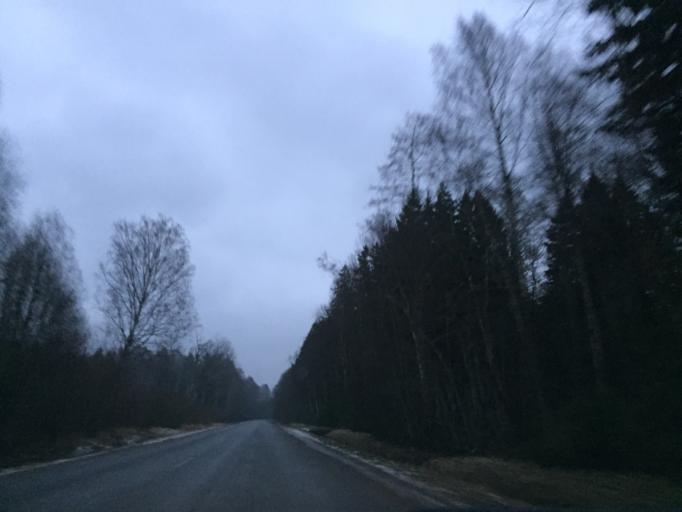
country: EE
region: Saare
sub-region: Kuressaare linn
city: Kuressaare
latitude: 58.5740
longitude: 22.6596
